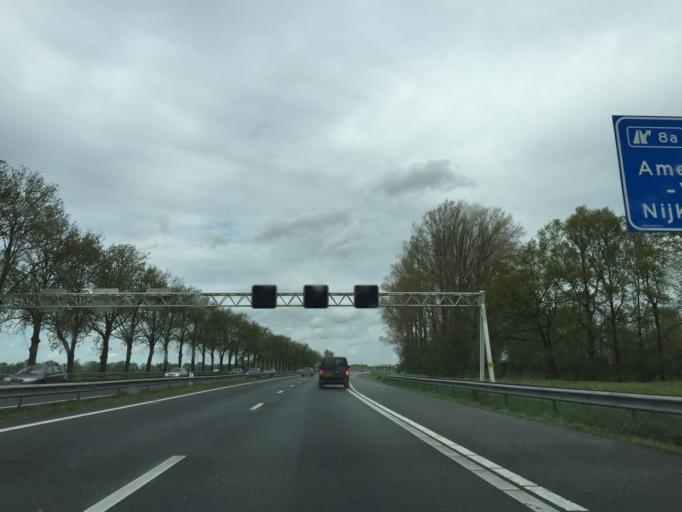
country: NL
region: Gelderland
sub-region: Gemeente Nijkerk
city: Nijkerk
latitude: 52.2037
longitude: 5.4395
